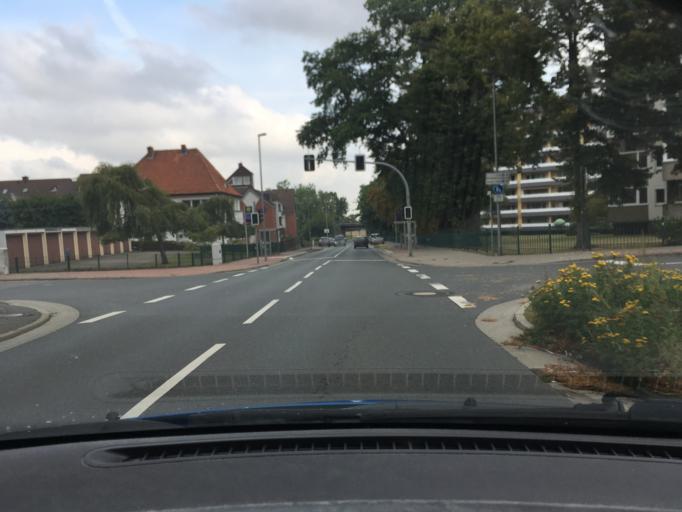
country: DE
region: Lower Saxony
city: Barsinghausen
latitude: 52.3068
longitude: 9.4601
